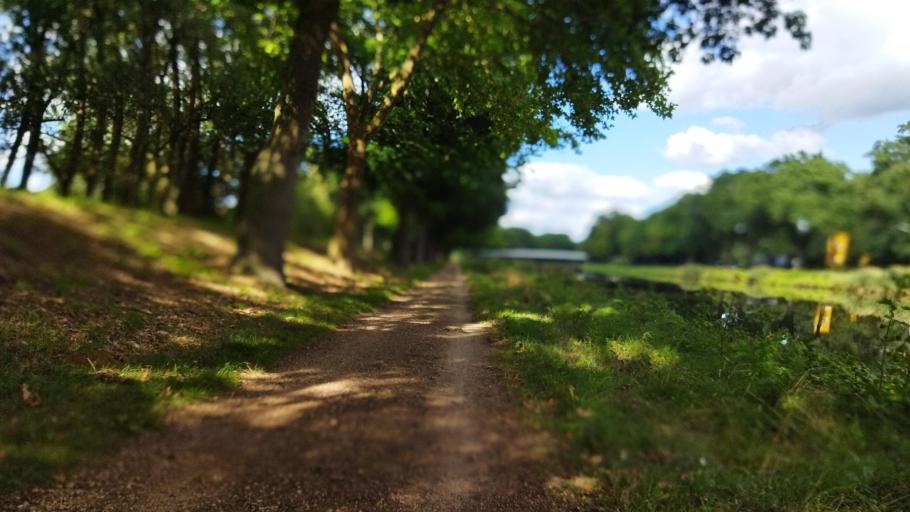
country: DE
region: Lower Saxony
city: Lingen
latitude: 52.4897
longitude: 7.2954
